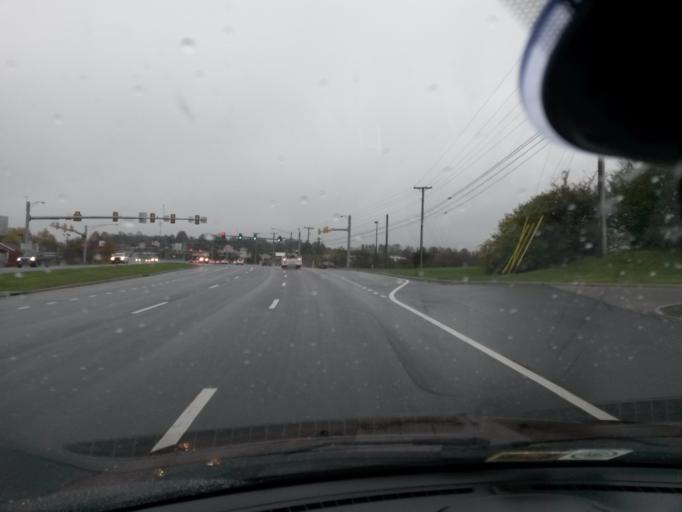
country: US
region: Virginia
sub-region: Montgomery County
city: Merrimac
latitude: 37.1626
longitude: -80.4234
